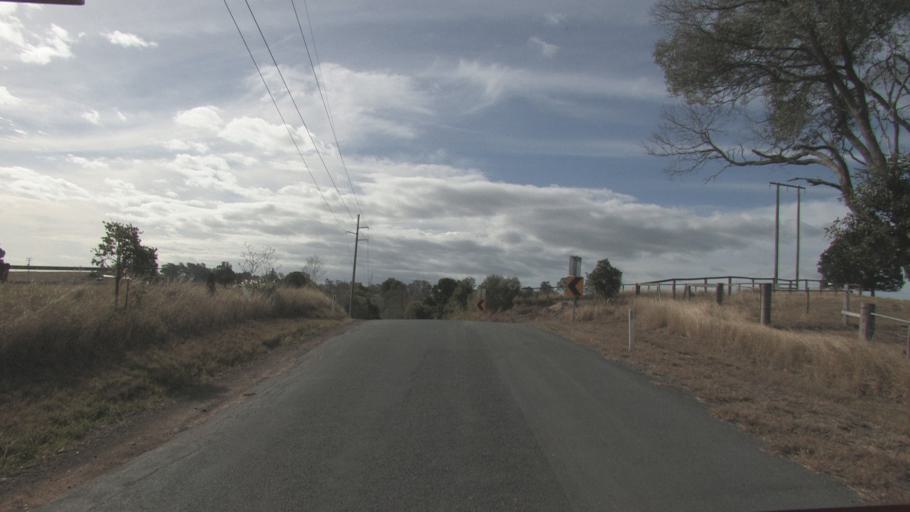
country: AU
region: Queensland
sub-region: Logan
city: Cedar Vale
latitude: -27.9047
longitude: 153.0145
